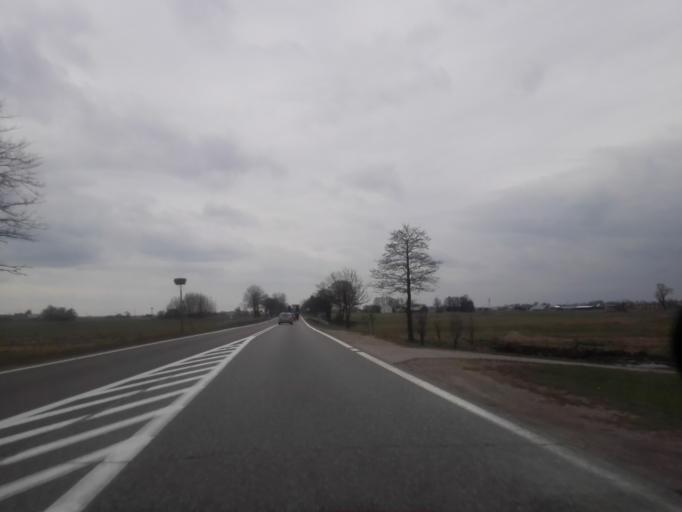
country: PL
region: Podlasie
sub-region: Powiat augustowski
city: Augustow
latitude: 53.8274
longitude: 22.9501
